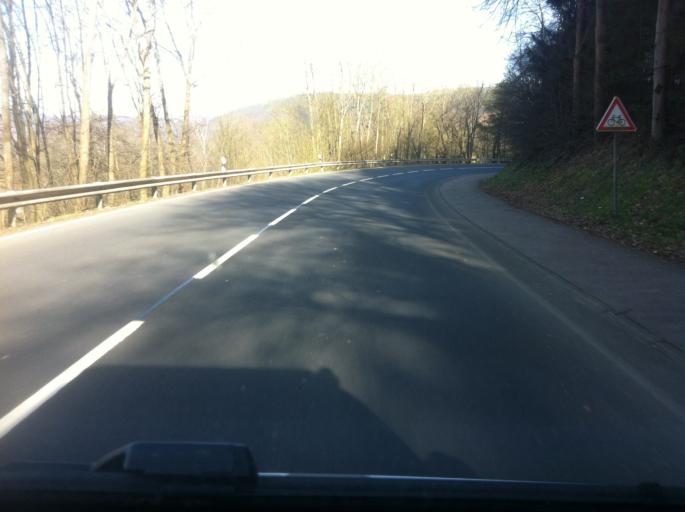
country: DE
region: North Rhine-Westphalia
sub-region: Regierungsbezirk Koln
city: Simmerath
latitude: 50.6144
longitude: 6.3736
